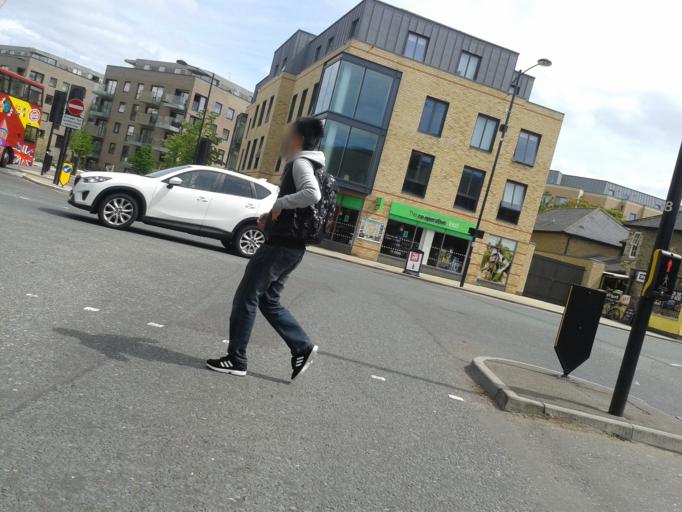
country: GB
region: England
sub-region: Cambridgeshire
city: Cambridge
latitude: 52.1923
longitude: 0.1334
